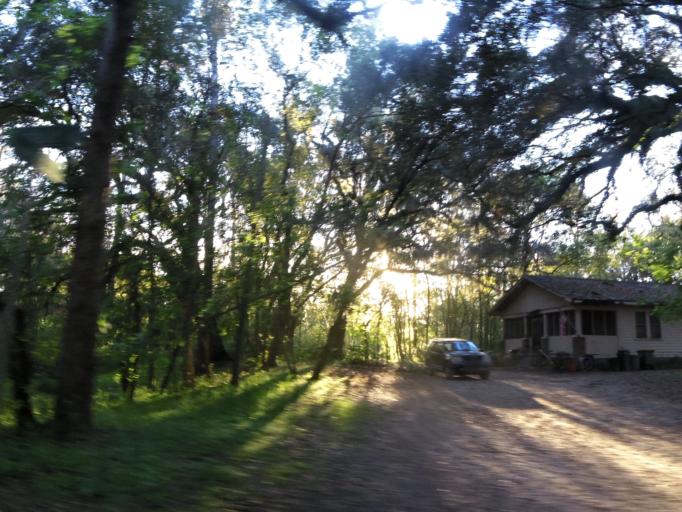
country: US
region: Florida
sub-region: Duval County
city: Jacksonville
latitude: 30.3362
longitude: -81.7042
